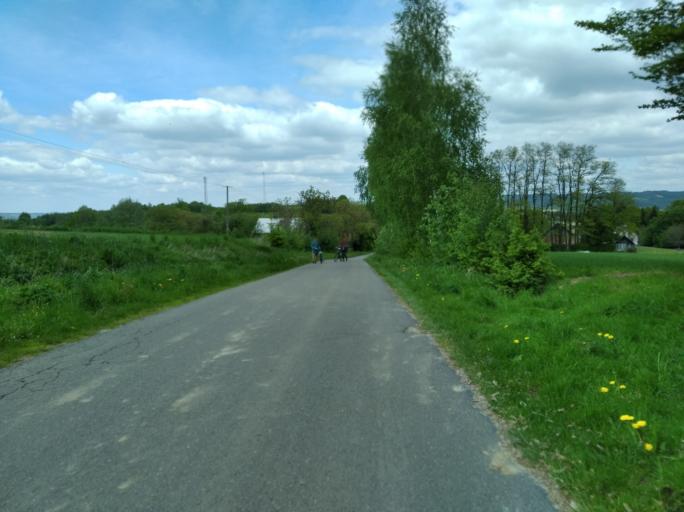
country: PL
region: Subcarpathian Voivodeship
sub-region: Powiat ropczycko-sedziszowski
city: Wielopole Skrzynskie
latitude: 49.9321
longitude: 21.6008
